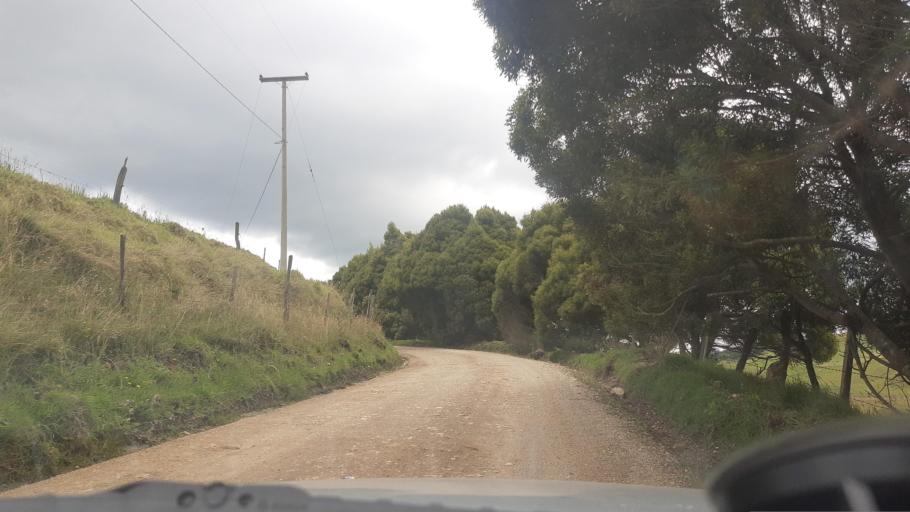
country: CO
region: Cundinamarca
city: Suesca
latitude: 5.1404
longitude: -73.7926
